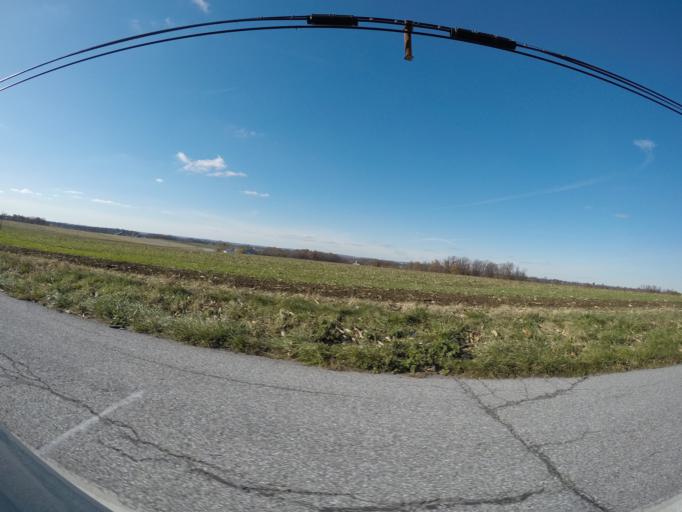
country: US
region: Pennsylvania
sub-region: Chester County
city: Oxford
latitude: 39.8305
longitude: -75.9528
